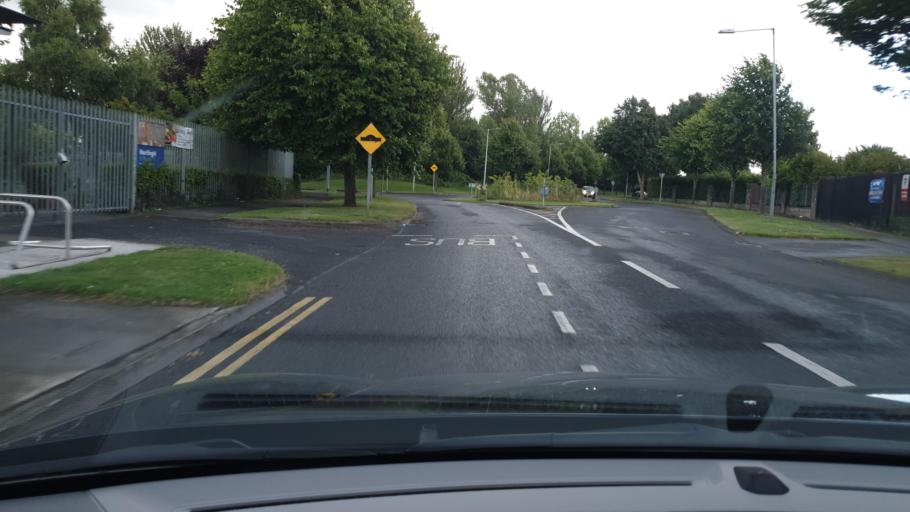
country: IE
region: Leinster
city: Clondalkin
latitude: 53.3232
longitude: -6.4247
